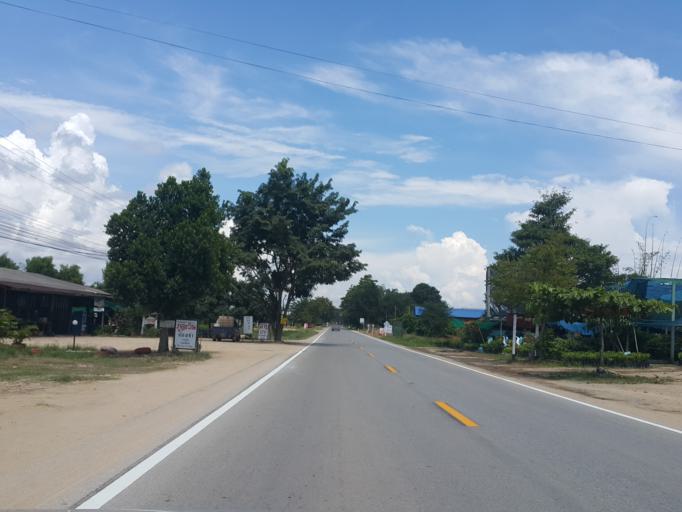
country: TH
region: Chiang Mai
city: Phrao
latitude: 19.2430
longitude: 99.1854
